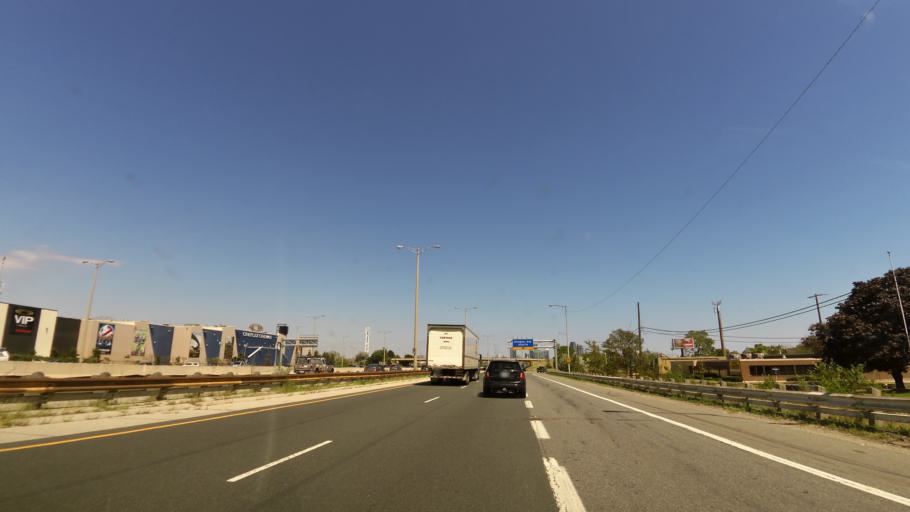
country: CA
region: Ontario
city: Etobicoke
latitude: 43.6194
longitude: -79.5170
